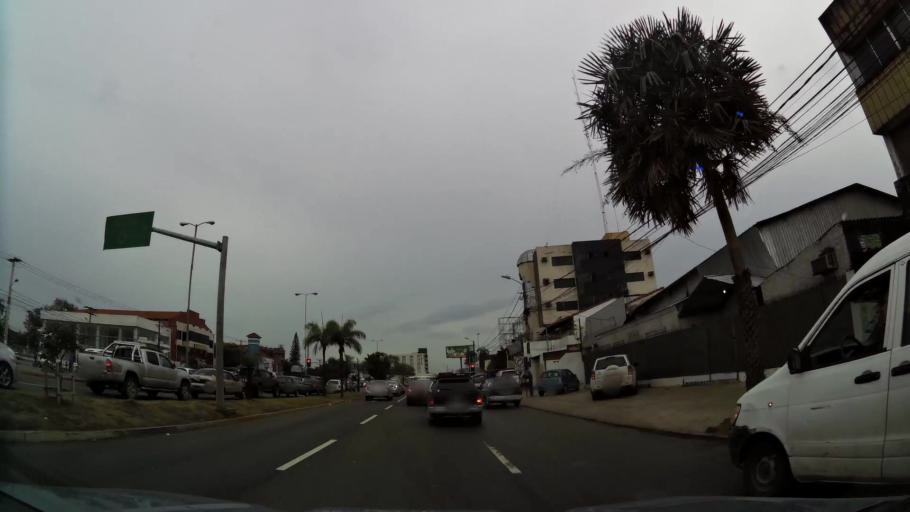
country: BO
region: Santa Cruz
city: Santa Cruz de la Sierra
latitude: -17.8005
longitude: -63.1849
